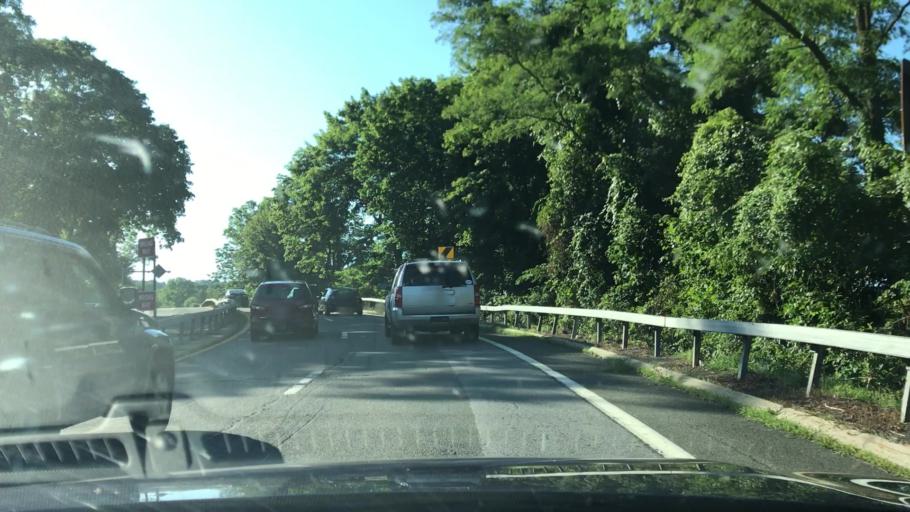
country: US
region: New York
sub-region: Westchester County
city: Hawthorne
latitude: 41.0968
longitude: -73.7934
